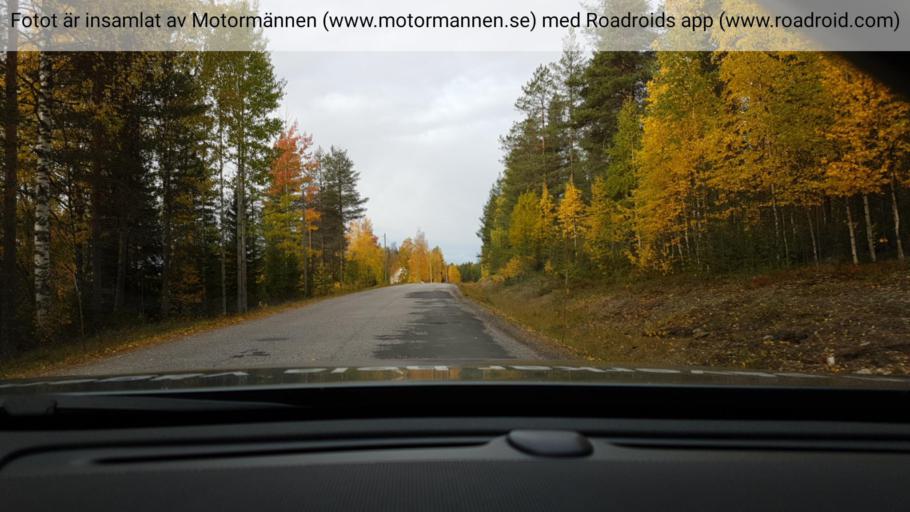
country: SE
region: Norrbotten
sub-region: Overkalix Kommun
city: OEverkalix
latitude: 66.2518
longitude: 23.1280
